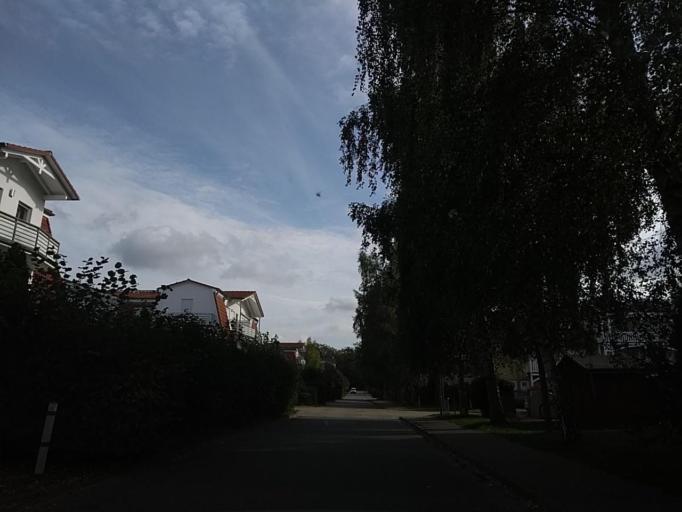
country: DE
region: Mecklenburg-Vorpommern
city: Seeheilbad Graal-Muritz
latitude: 54.2587
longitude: 12.2560
